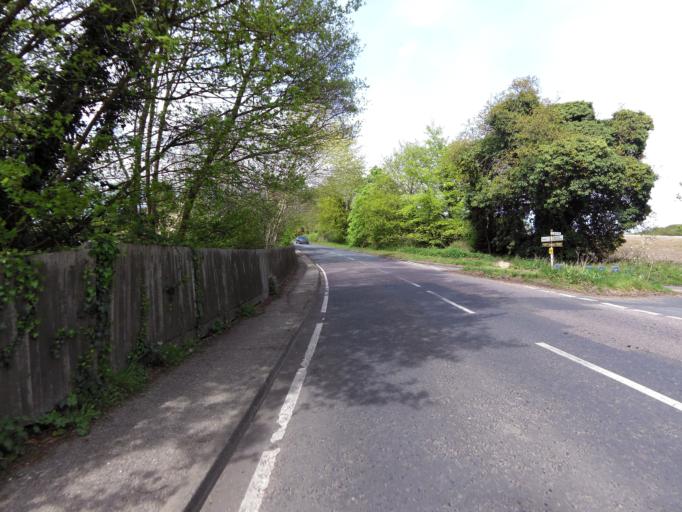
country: GB
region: England
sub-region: Suffolk
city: Ipswich
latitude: 51.9789
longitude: 1.1581
